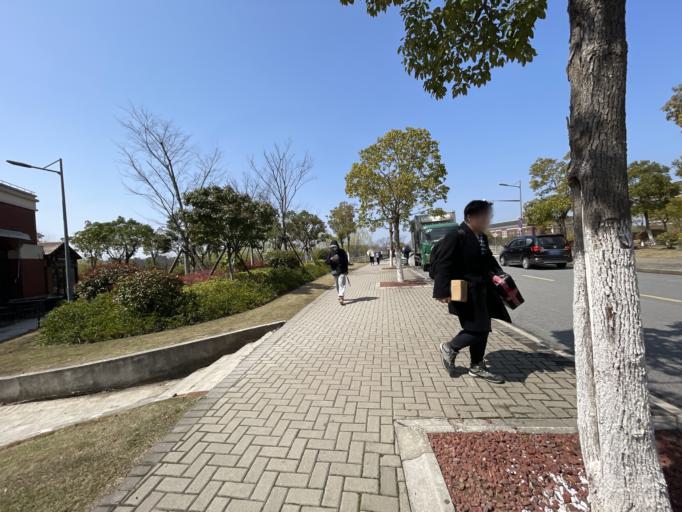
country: CN
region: Shanghai Shi
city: Shuyuan
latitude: 30.8924
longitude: 121.8861
